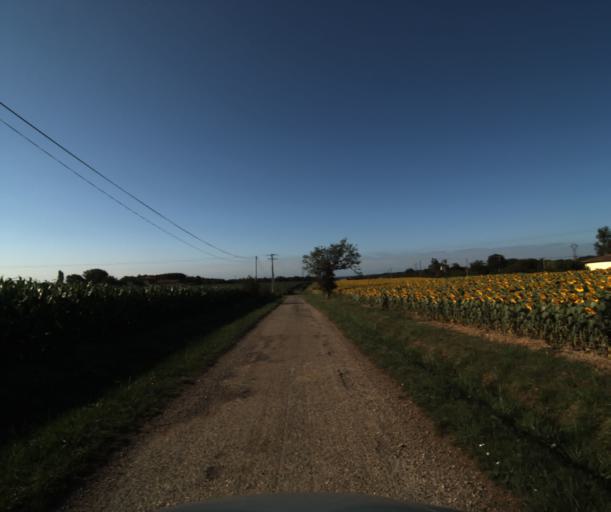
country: FR
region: Midi-Pyrenees
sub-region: Departement de la Haute-Garonne
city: Labarthe-sur-Leze
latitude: 43.4450
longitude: 1.3764
